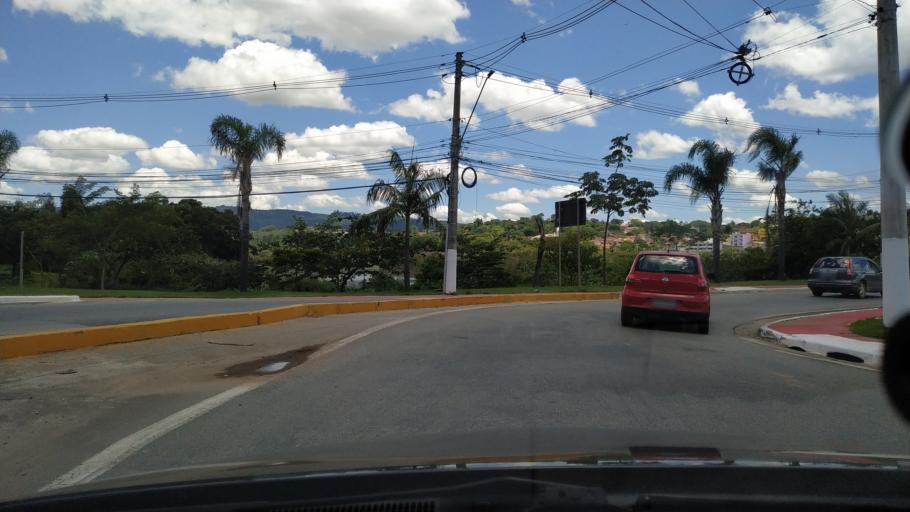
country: BR
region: Sao Paulo
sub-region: Santana De Parnaiba
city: Santana de Parnaiba
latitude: -23.4395
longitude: -46.9083
